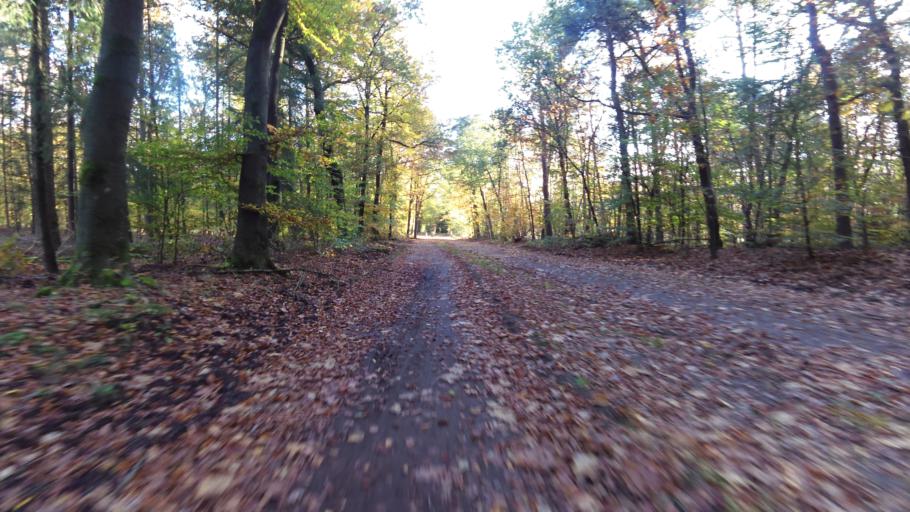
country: NL
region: Gelderland
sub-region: Gemeente Epe
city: Epe
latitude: 52.3742
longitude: 5.9846
